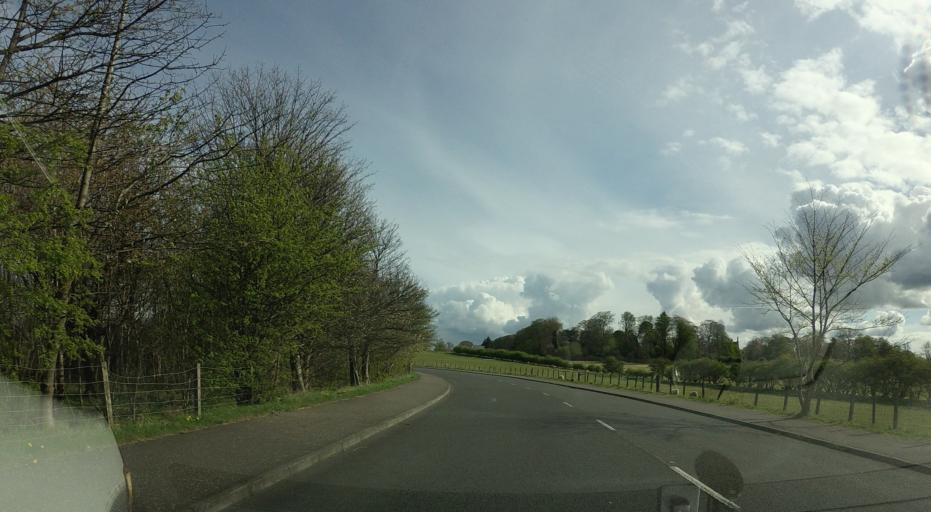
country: GB
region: Scotland
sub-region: Edinburgh
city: Colinton
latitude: 55.9746
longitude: -3.2771
